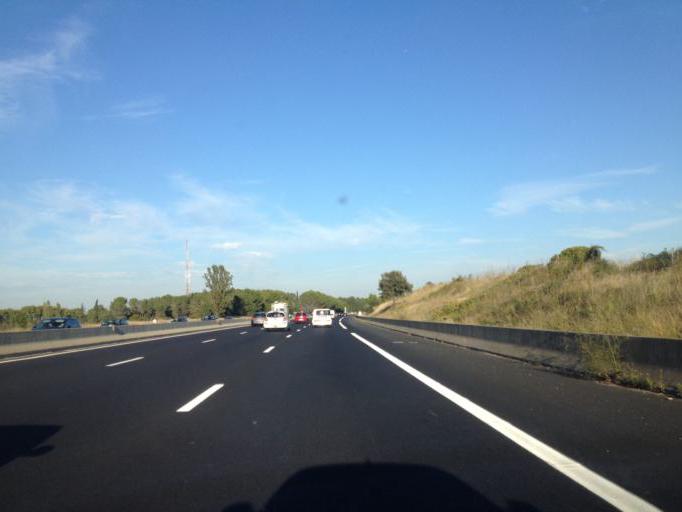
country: FR
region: Languedoc-Roussillon
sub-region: Departement de l'Herault
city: Valergues
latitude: 43.6872
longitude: 4.0547
